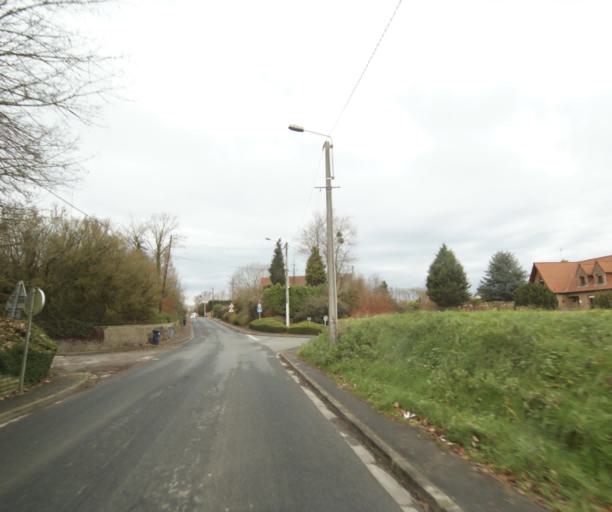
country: FR
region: Nord-Pas-de-Calais
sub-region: Departement du Nord
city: Saint-Saulve
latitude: 50.3610
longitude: 3.5670
